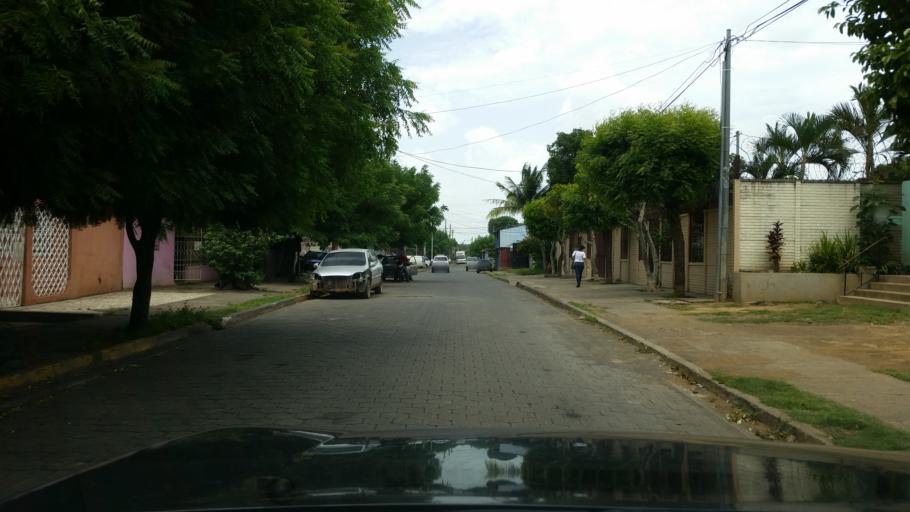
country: NI
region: Managua
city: Managua
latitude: 12.1471
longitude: -86.2150
